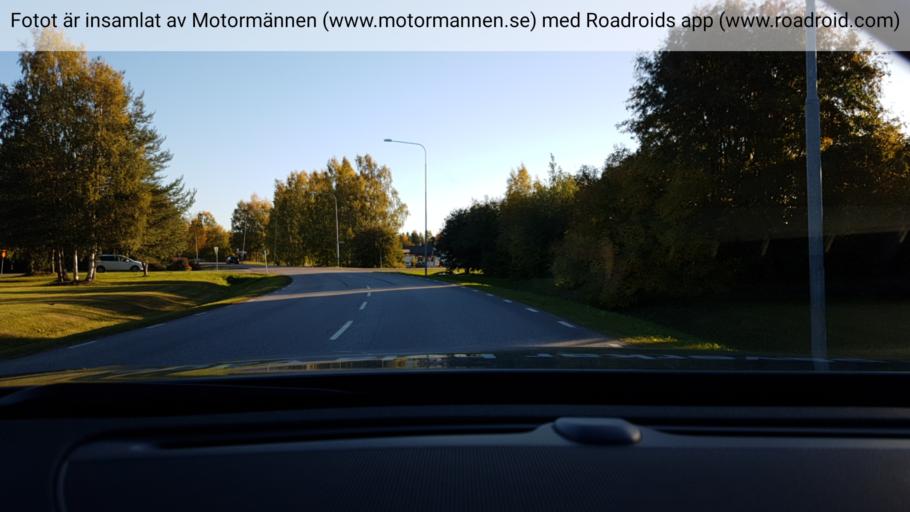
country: SE
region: Norrbotten
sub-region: Lulea Kommun
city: Sodra Sunderbyn
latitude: 65.6505
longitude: 21.9593
